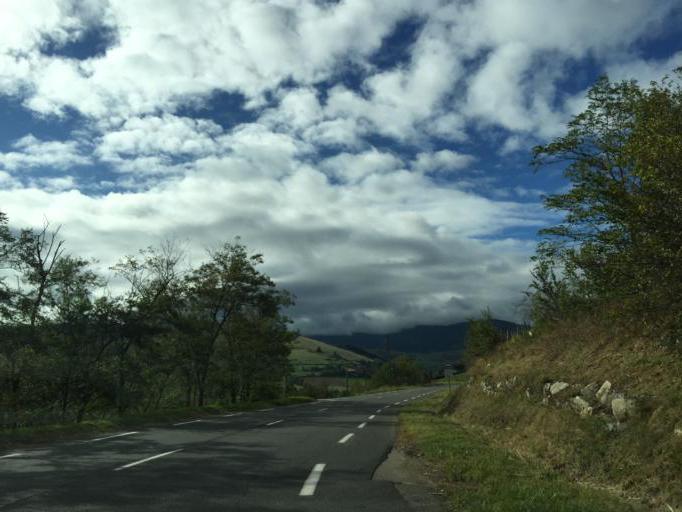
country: FR
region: Rhone-Alpes
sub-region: Departement de la Loire
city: Saint-Paul-en-Jarez
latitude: 45.4696
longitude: 4.5846
